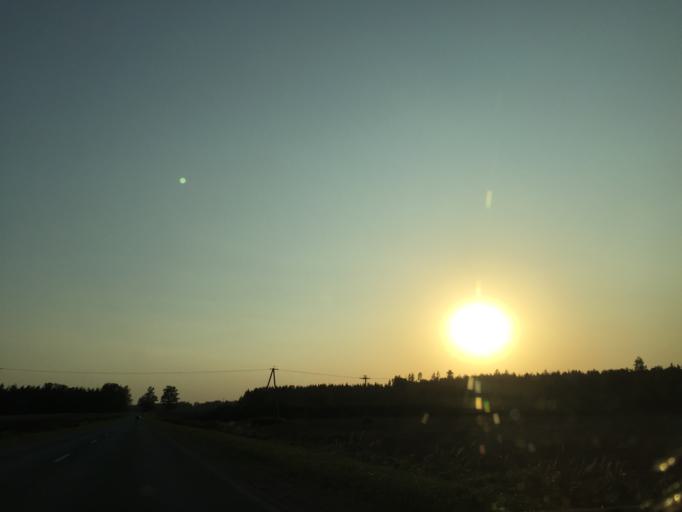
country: LV
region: Lielvarde
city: Lielvarde
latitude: 56.7762
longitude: 24.7810
